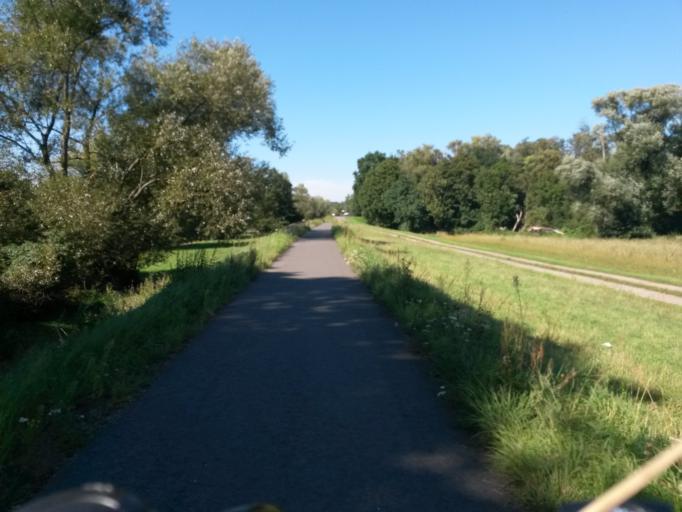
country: DE
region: Brandenburg
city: Schoneberg
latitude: 52.9476
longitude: 14.1110
